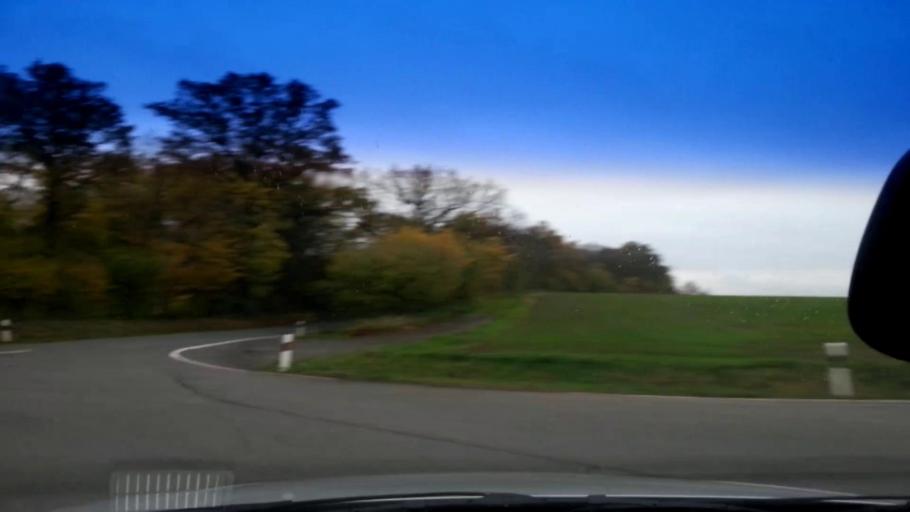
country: DE
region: Bavaria
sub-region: Upper Franconia
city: Schesslitz
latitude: 49.9643
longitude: 11.0204
